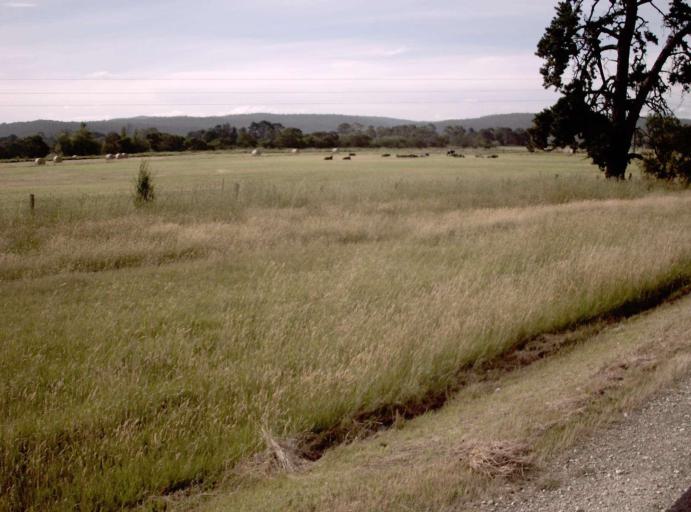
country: AU
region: Victoria
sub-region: Latrobe
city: Traralgon
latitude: -38.1041
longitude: 146.5932
